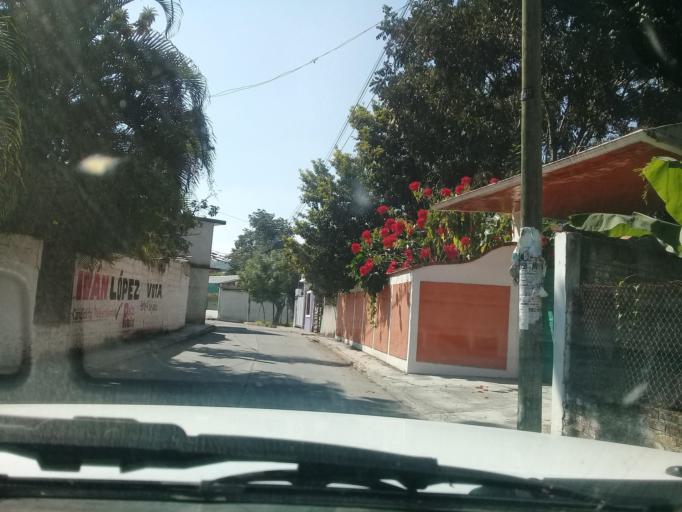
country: MX
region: Veracruz
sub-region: Emiliano Zapata
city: Plan del Rio
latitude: 19.4169
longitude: -96.6165
